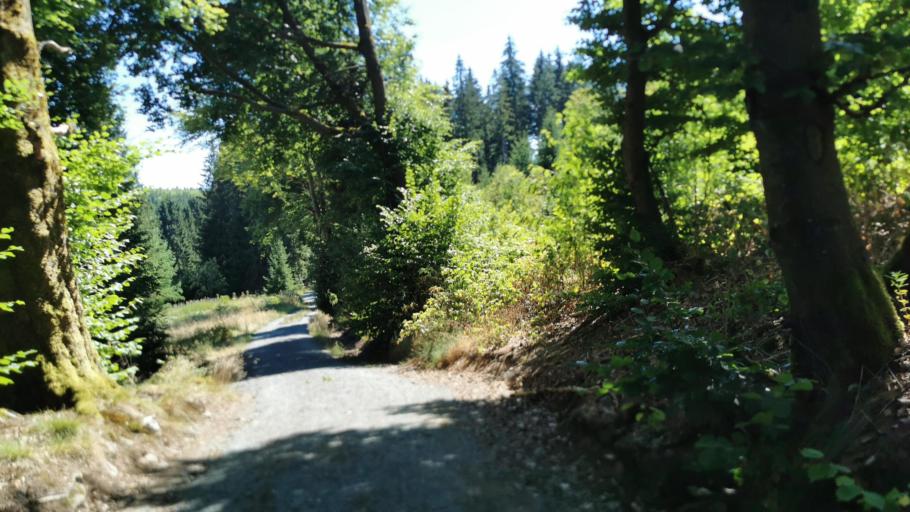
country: DE
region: Bavaria
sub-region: Upper Franconia
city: Pressig
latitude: 50.4119
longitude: 11.2923
